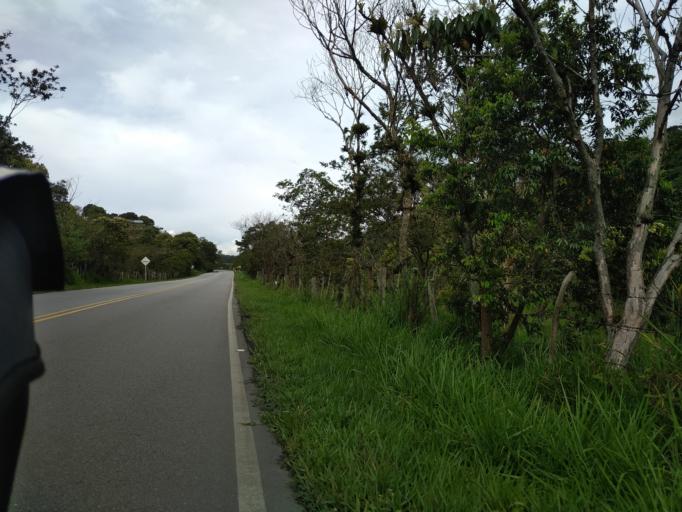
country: CO
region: Santander
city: Suaita
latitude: 6.1066
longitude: -73.3677
